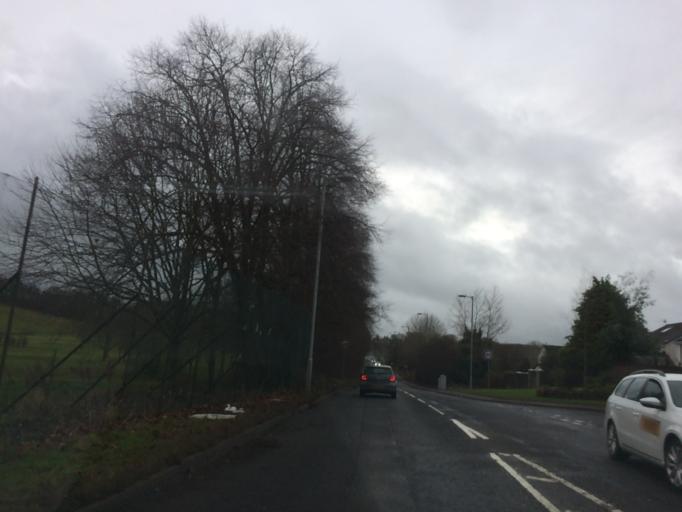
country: GB
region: Scotland
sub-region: East Renfrewshire
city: Newton Mearns
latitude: 55.7982
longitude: -4.3259
